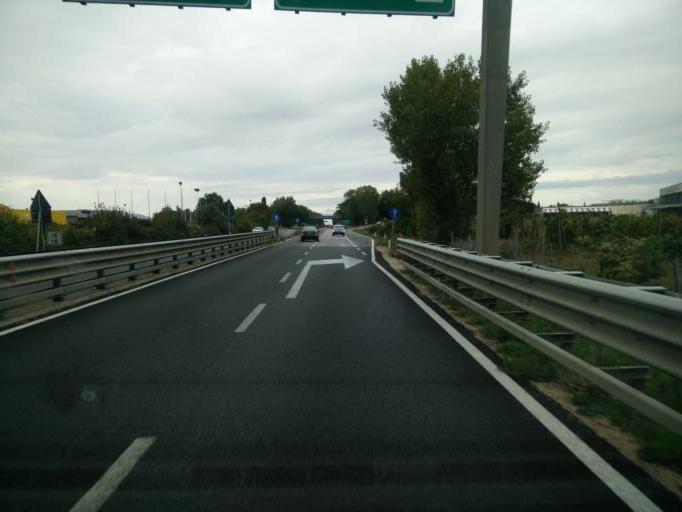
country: IT
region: Tuscany
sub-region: Provincia di Siena
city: Staggia
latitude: 43.4123
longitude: 11.1637
